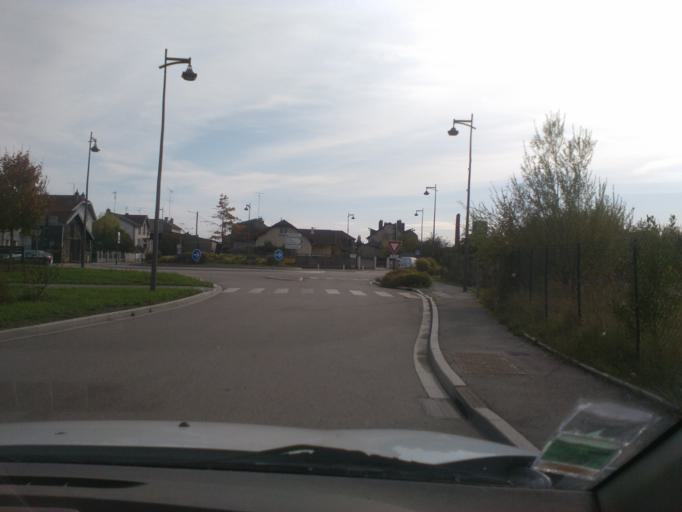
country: FR
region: Lorraine
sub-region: Departement des Vosges
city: Rambervillers
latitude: 48.3440
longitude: 6.6289
